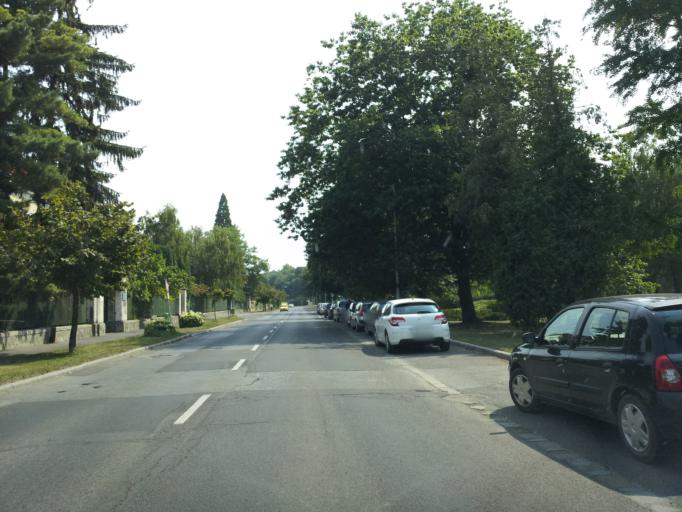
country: HU
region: Vas
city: Szombathely
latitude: 47.2279
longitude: 16.6052
